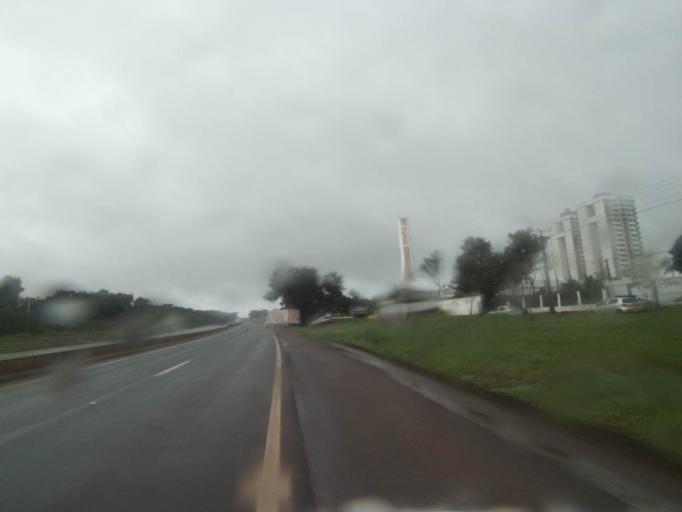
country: PY
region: Alto Parana
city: Ciudad del Este
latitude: -25.5096
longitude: -54.5770
